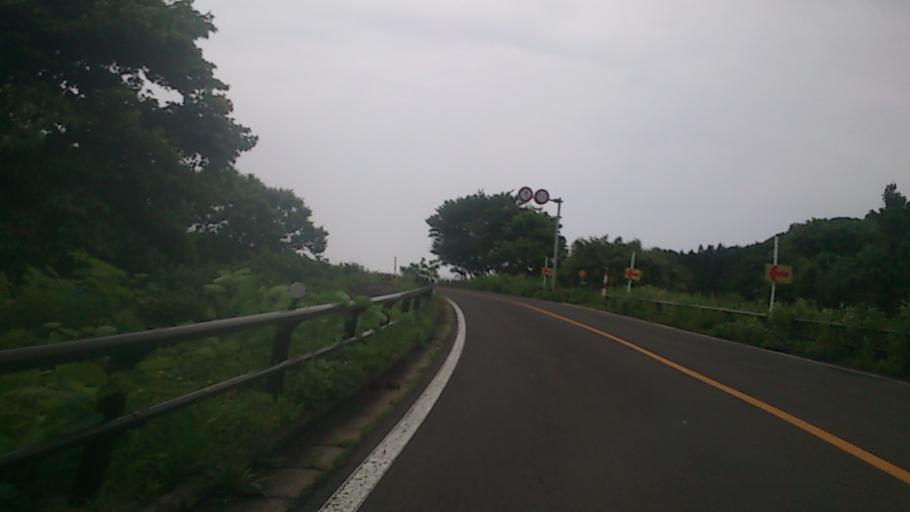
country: JP
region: Akita
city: Noshiromachi
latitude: 40.3824
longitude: 139.9997
